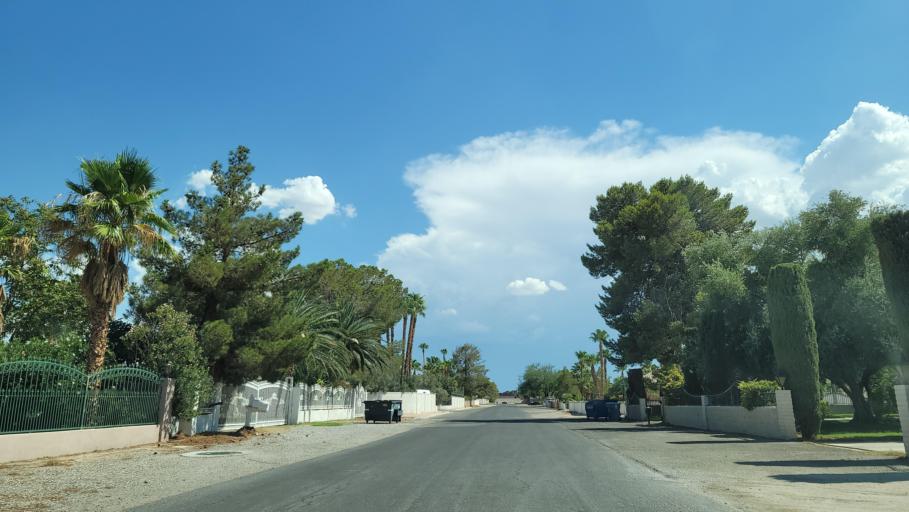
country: US
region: Nevada
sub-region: Clark County
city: Spring Valley
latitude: 36.1335
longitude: -115.2273
